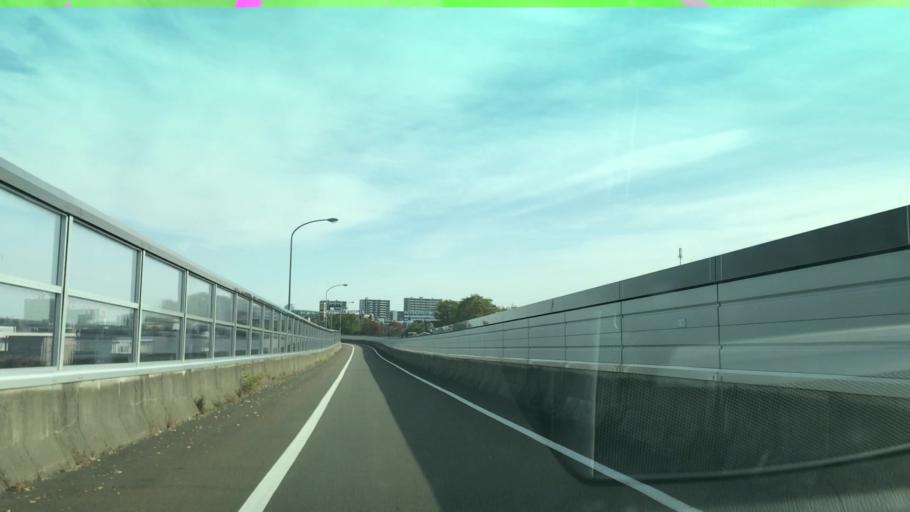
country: JP
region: Hokkaido
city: Sapporo
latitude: 43.0912
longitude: 141.2630
